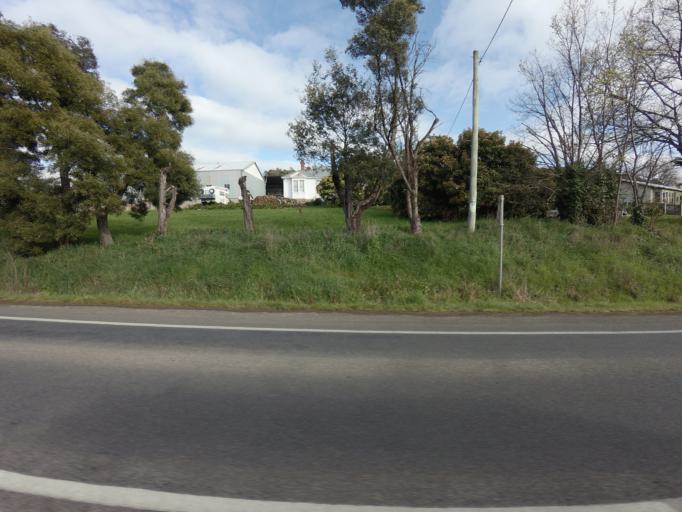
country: AU
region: Tasmania
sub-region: Huon Valley
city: Huonville
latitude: -43.0439
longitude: 147.0437
